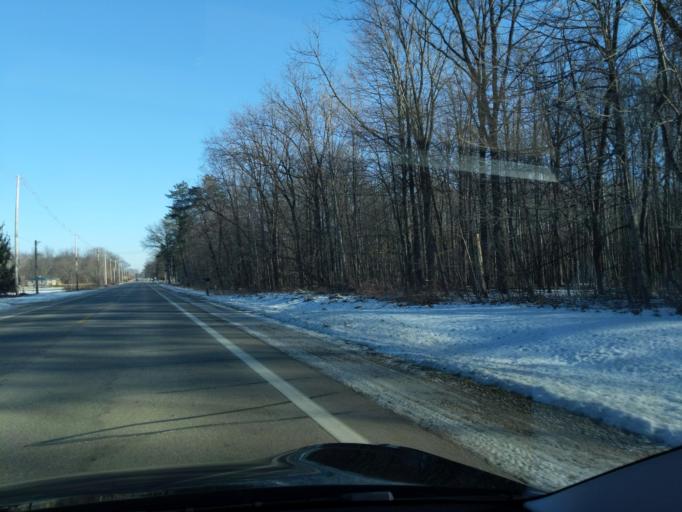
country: US
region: Michigan
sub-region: Ingham County
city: Stockbridge
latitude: 42.3936
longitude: -84.2828
